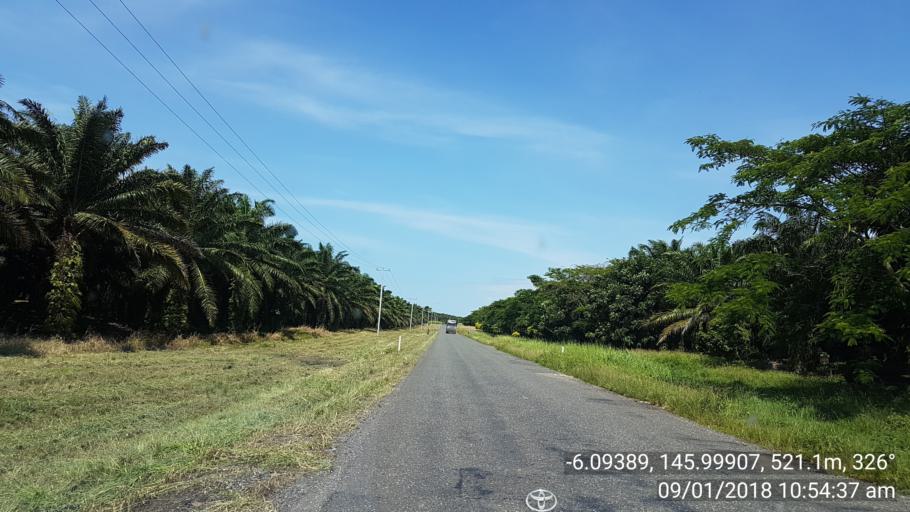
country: PG
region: Eastern Highlands
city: Kainantu
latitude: -6.0938
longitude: 145.9992
